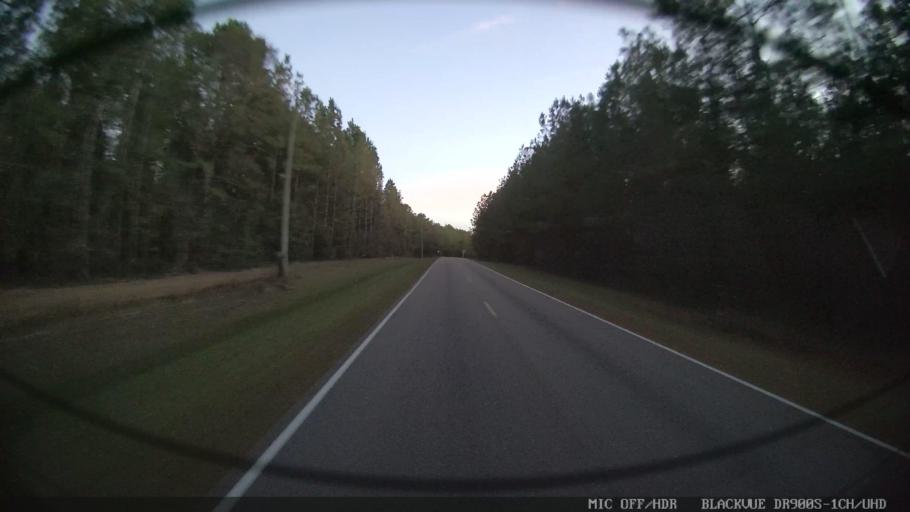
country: US
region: Mississippi
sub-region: Perry County
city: New Augusta
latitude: 31.1055
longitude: -89.1927
